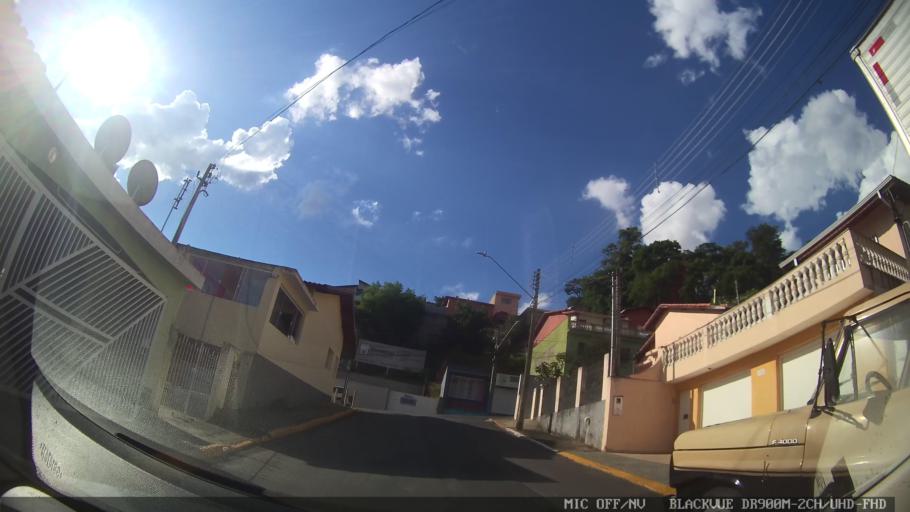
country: BR
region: Minas Gerais
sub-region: Extrema
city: Extrema
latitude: -22.8551
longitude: -46.3214
